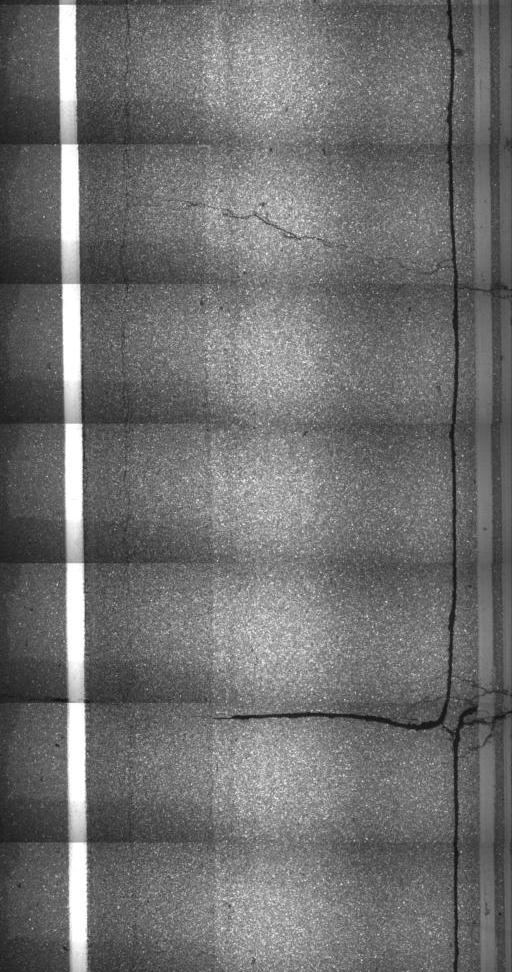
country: US
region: Vermont
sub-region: Bennington County
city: Arlington
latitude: 43.0279
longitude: -73.1850
